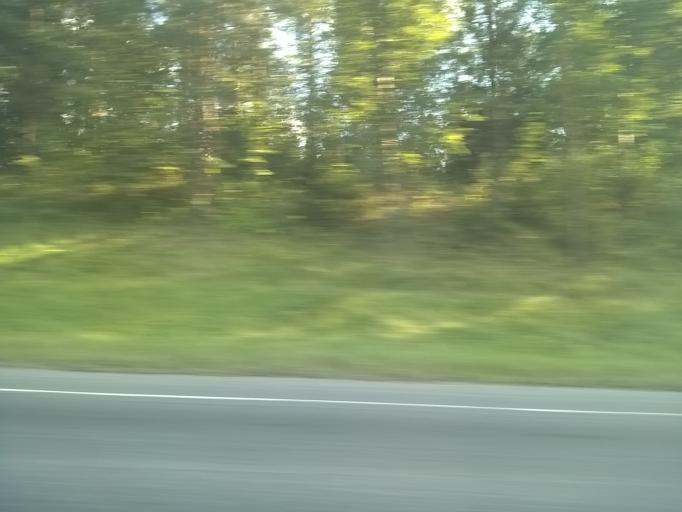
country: FI
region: Pirkanmaa
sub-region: Tampere
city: Tampere
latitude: 61.5057
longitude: 23.8414
